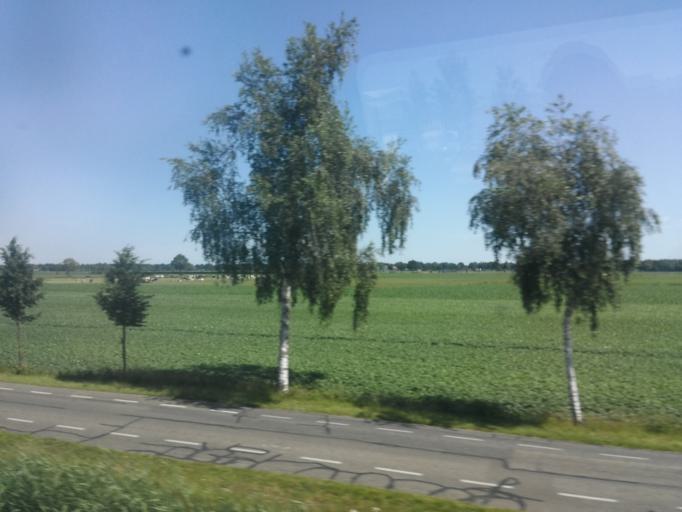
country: NL
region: Overijssel
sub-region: Gemeente Staphorst
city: Staphorst
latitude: 52.6325
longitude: 6.2334
